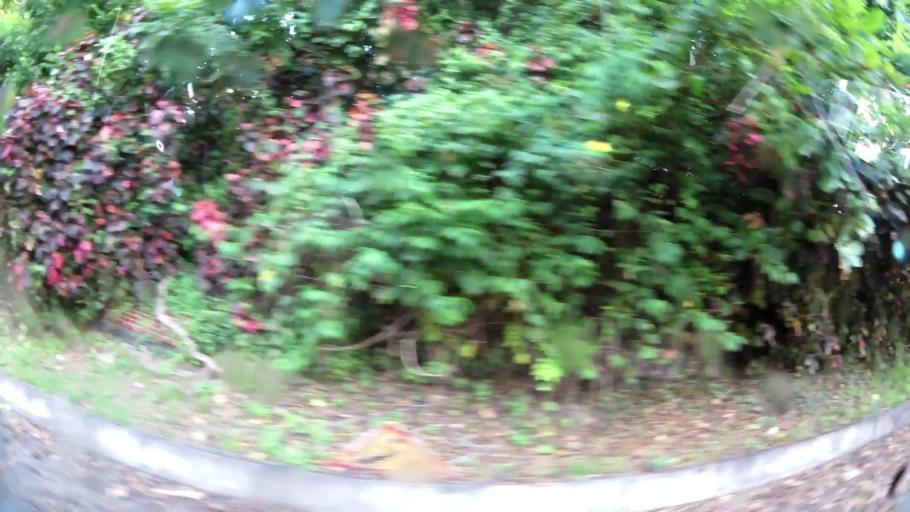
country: MQ
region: Martinique
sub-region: Martinique
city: Fort-de-France
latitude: 14.6296
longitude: -61.0697
